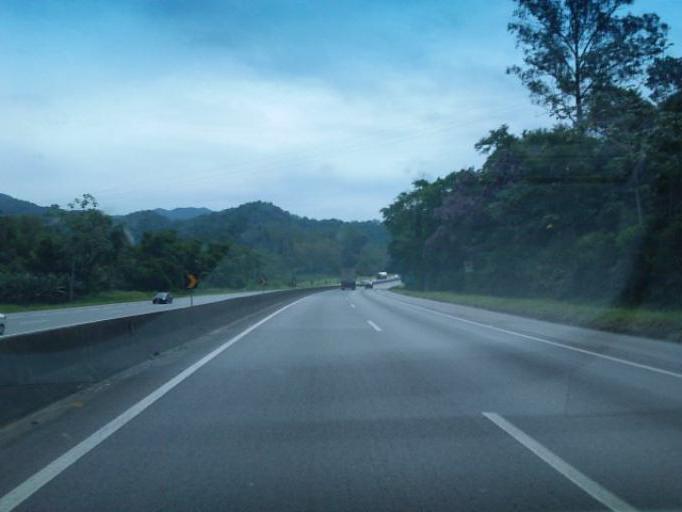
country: BR
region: Sao Paulo
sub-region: Miracatu
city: Miracatu
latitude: -24.3199
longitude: -47.5331
